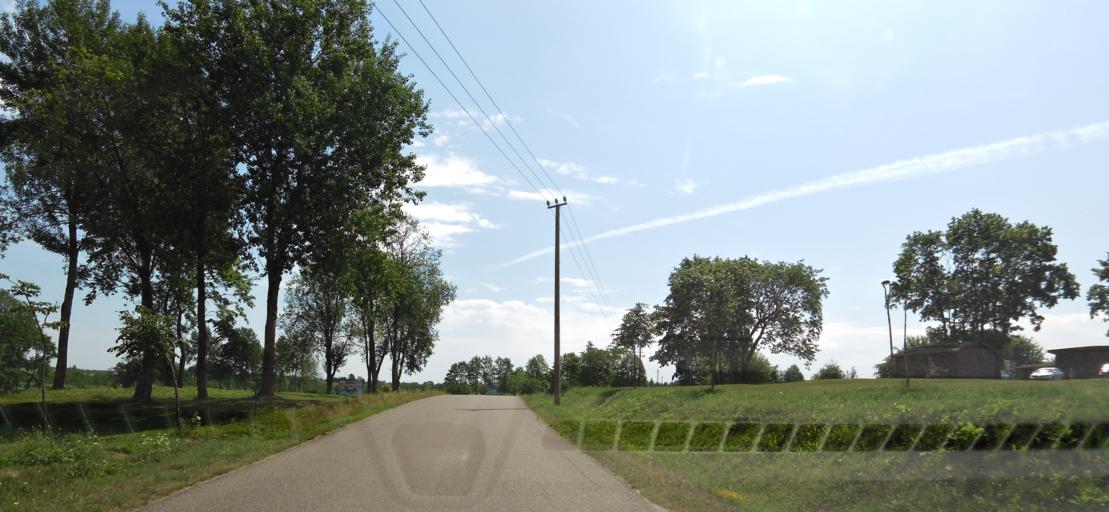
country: LT
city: Nemencine
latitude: 54.9110
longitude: 25.3123
